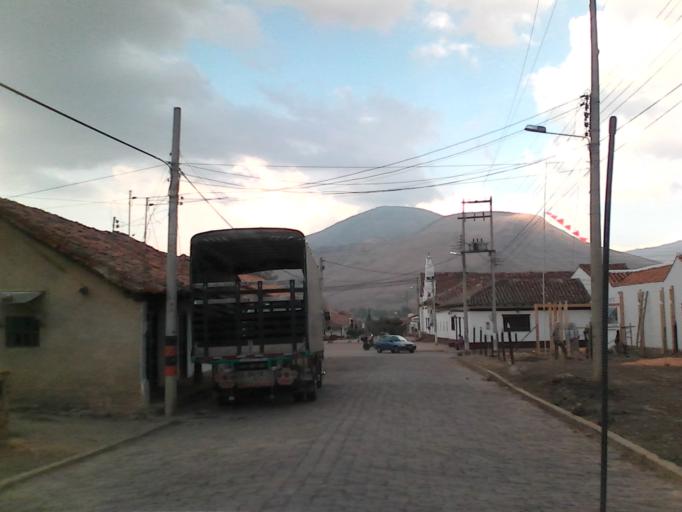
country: CO
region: Boyaca
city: Sachica
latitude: 5.5829
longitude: -73.5426
